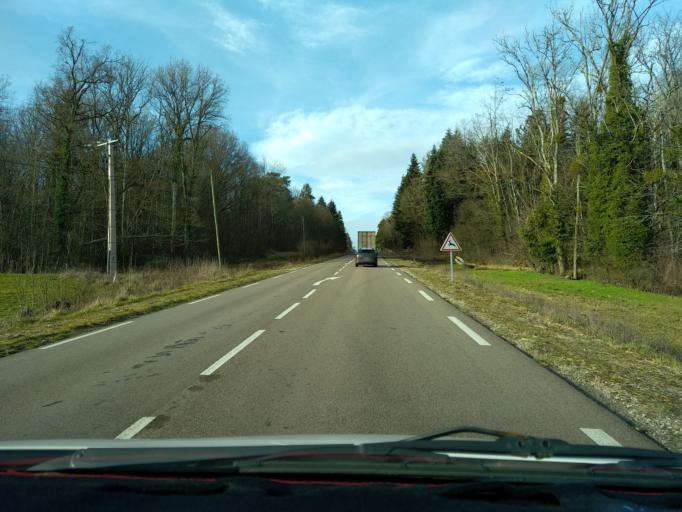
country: FR
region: Franche-Comte
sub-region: Departement de la Haute-Saone
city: Gray
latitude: 47.3998
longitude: 5.6447
